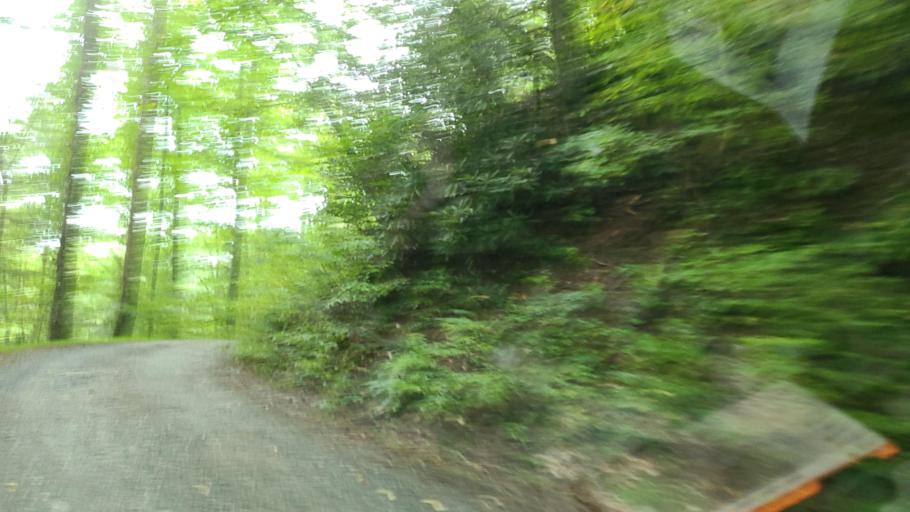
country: US
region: Georgia
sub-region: Gilmer County
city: Ellijay
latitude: 34.8065
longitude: -84.5596
